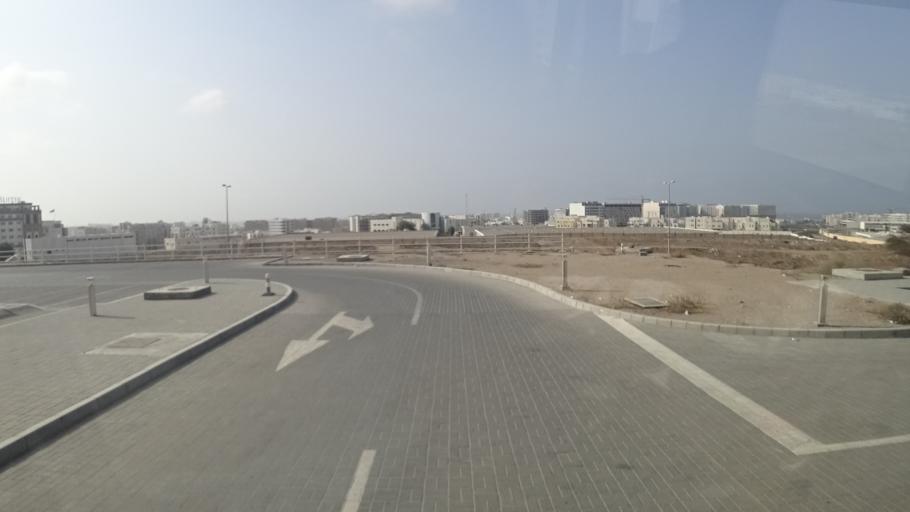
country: OM
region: Muhafazat Masqat
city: Bawshar
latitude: 23.5795
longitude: 58.4149
